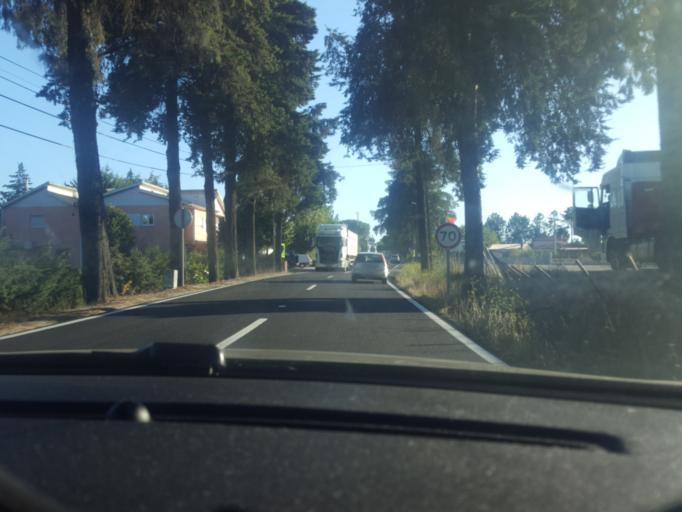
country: PT
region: Viseu
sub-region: Mangualde
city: Mangualde
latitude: 40.5866
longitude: -7.8032
